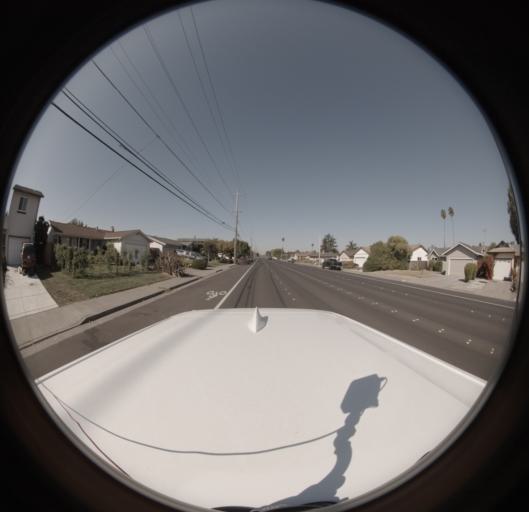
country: US
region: California
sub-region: Sonoma County
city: Petaluma
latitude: 38.2533
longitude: -122.6133
